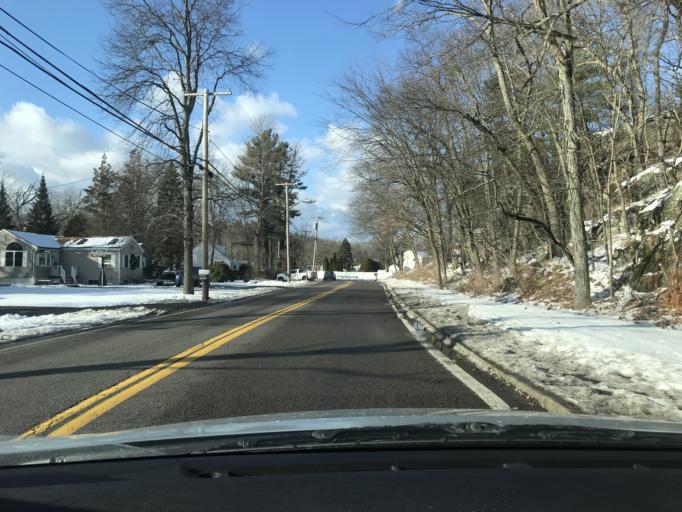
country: US
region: Massachusetts
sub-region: Essex County
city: Saugus
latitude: 42.4961
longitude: -71.0262
